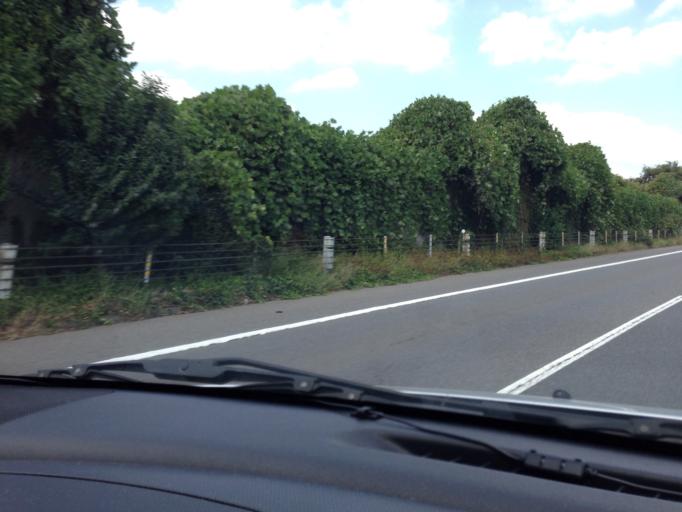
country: JP
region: Ibaraki
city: Naka
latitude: 36.1215
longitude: 140.1863
